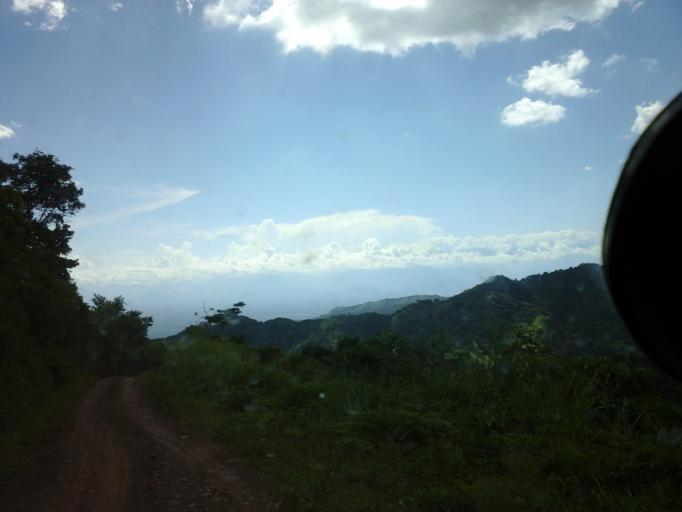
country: CO
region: Cesar
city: San Diego
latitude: 10.2702
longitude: -73.0829
